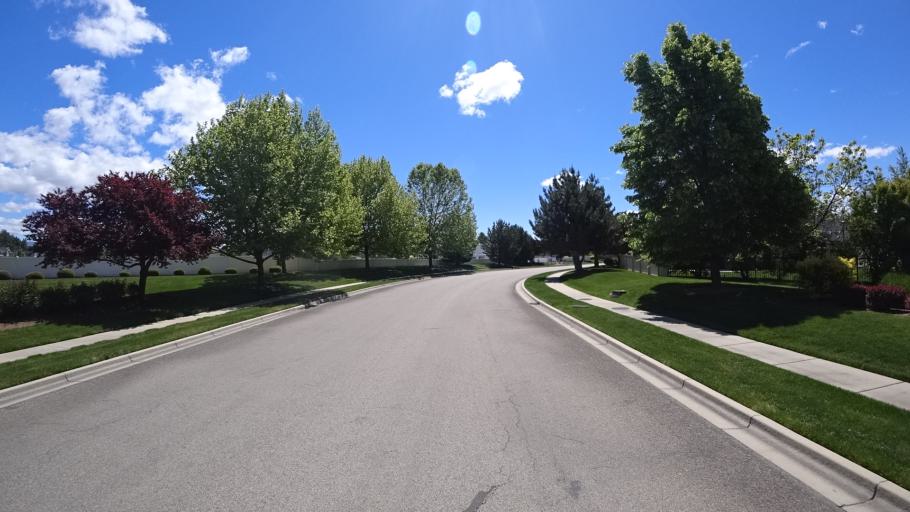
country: US
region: Idaho
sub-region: Ada County
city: Meridian
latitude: 43.6296
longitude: -116.3410
